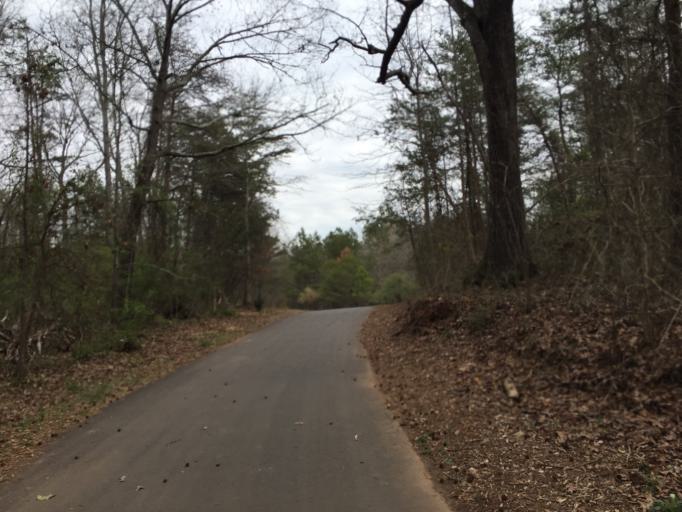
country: US
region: South Carolina
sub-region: Greenville County
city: Mauldin
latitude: 34.7793
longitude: -82.3578
